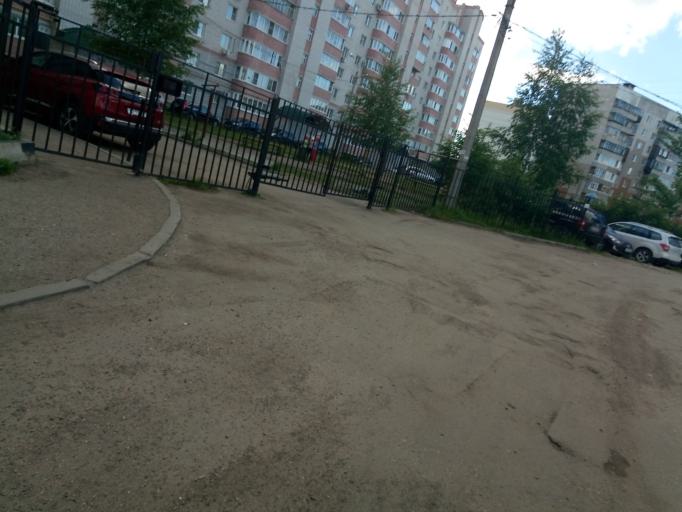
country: RU
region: Jaroslavl
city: Yaroslavl
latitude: 57.6387
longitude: 39.9504
